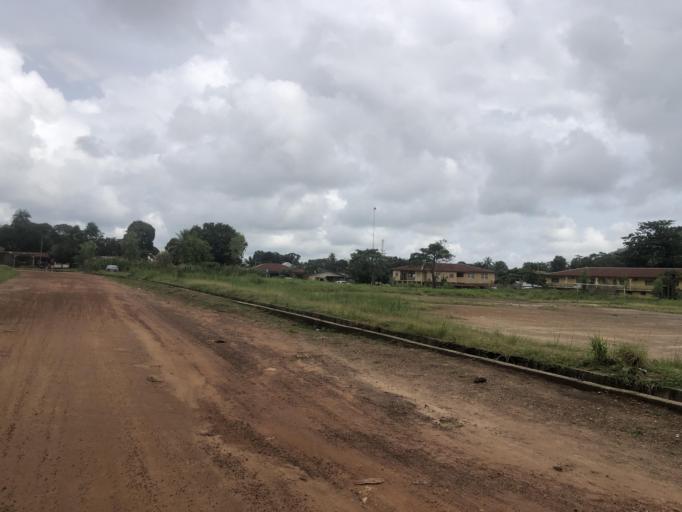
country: SL
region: Northern Province
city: Makeni
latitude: 8.8881
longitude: -12.0564
